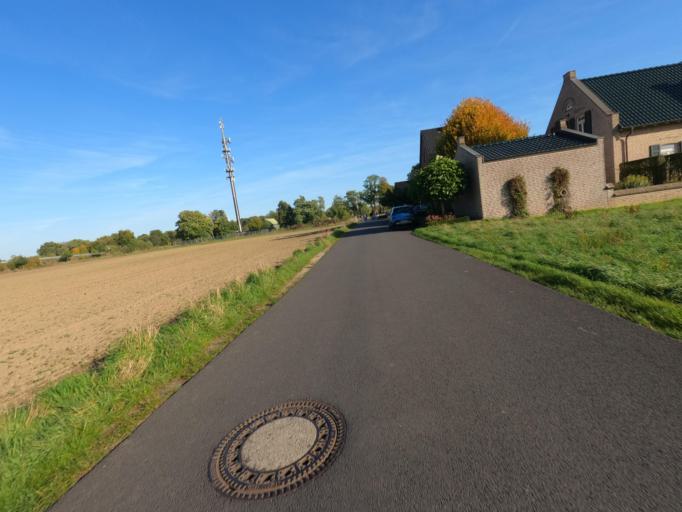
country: DE
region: North Rhine-Westphalia
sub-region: Regierungsbezirk Koln
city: Wassenberg
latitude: 51.1220
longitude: 6.1988
